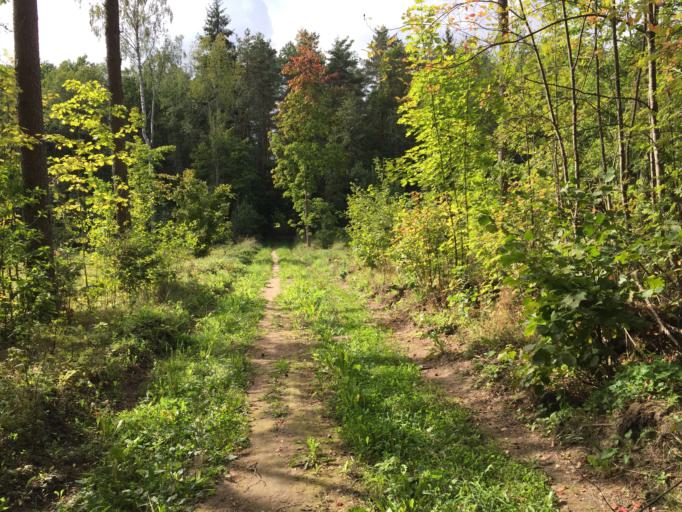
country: LV
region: Limbazu Rajons
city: Limbazi
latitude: 57.3936
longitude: 24.6940
